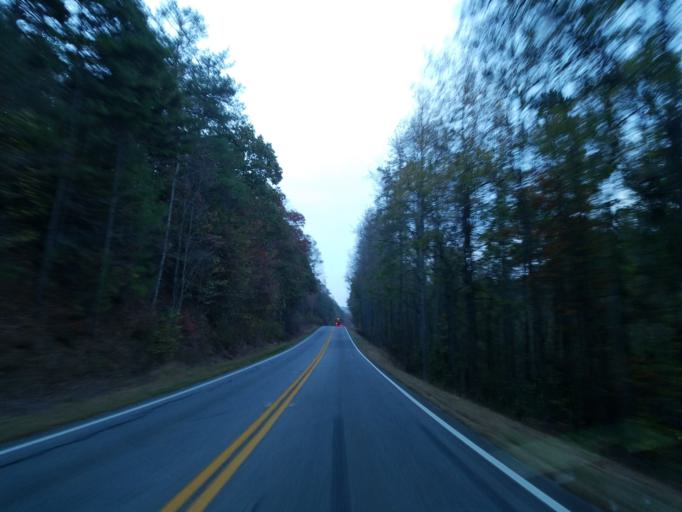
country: US
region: Georgia
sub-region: Pickens County
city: Jasper
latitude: 34.5400
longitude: -84.5797
